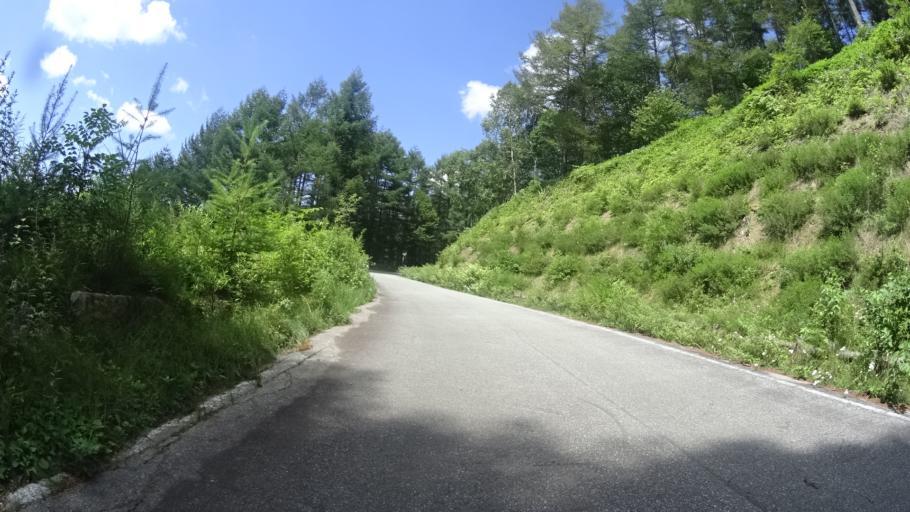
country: JP
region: Yamanashi
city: Enzan
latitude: 35.8381
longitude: 138.6399
